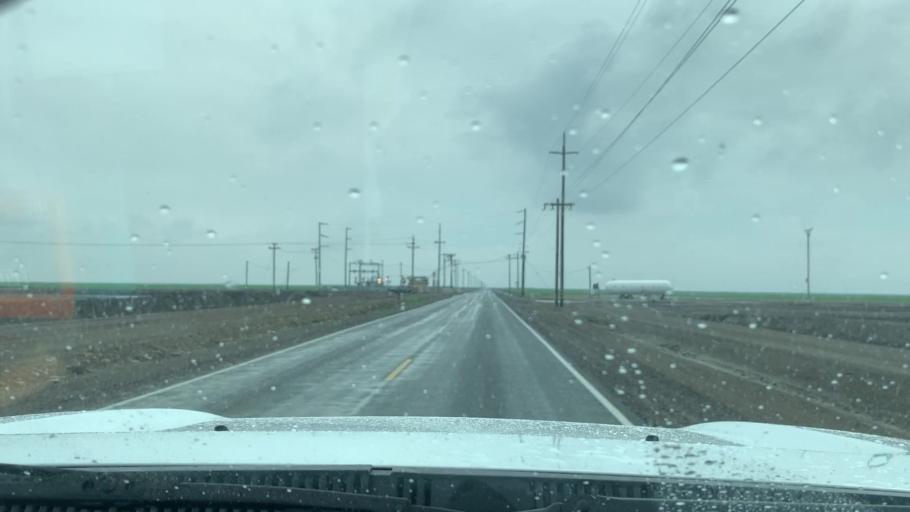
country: US
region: California
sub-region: Kings County
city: Corcoran
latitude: 35.9940
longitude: -119.5720
